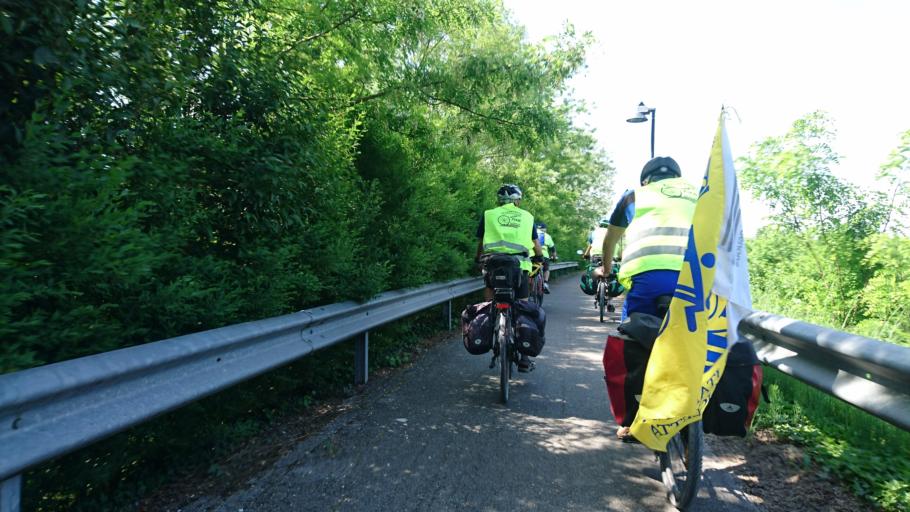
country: IT
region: Veneto
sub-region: Provincia di Padova
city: Vigodarzere
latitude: 45.4439
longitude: 11.8878
